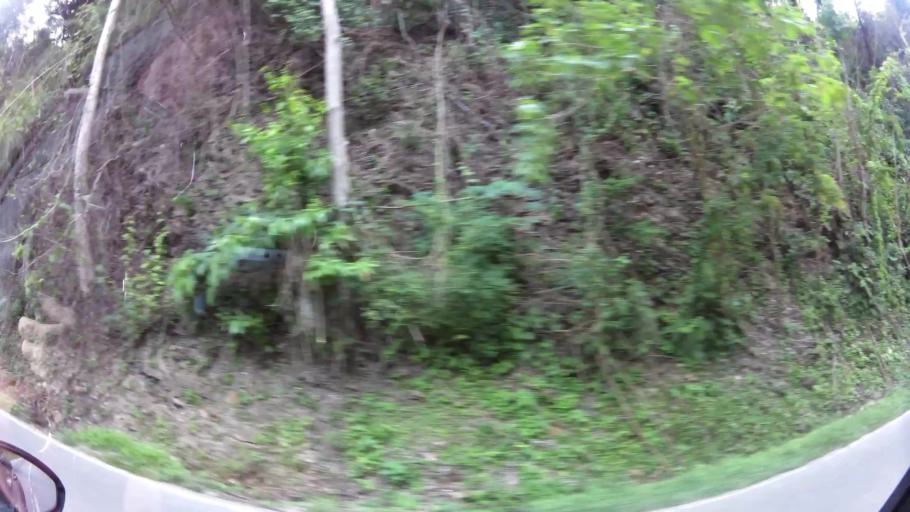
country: TT
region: Diego Martin
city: Petit Valley
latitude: 10.7257
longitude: -61.4939
